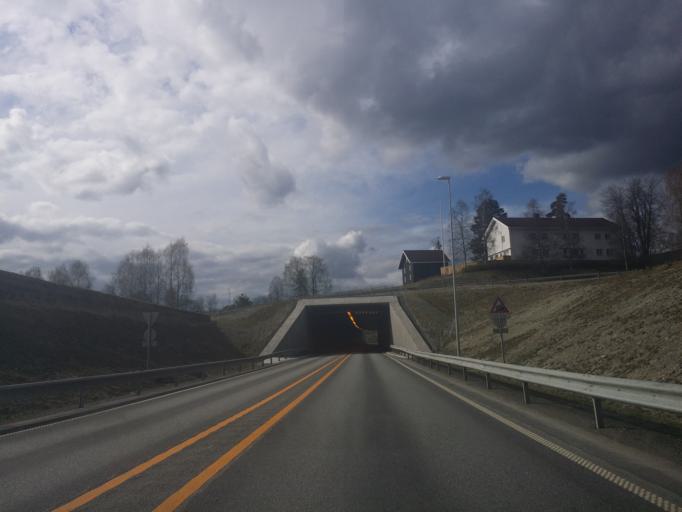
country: NO
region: Buskerud
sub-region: Modum
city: Vikersund
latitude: 60.2430
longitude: 9.9163
